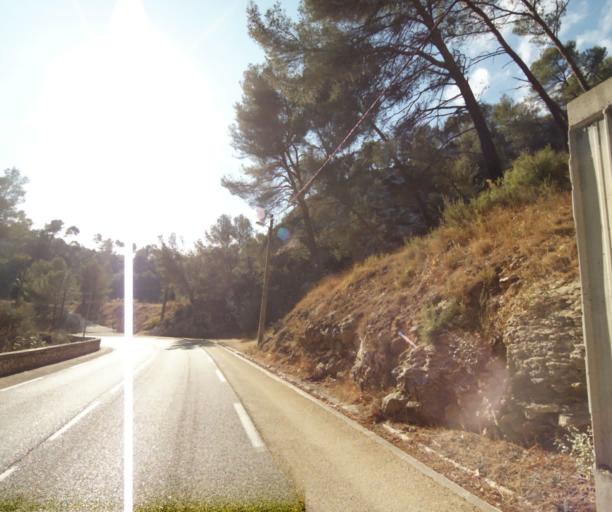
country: FR
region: Provence-Alpes-Cote d'Azur
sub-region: Departement des Bouches-du-Rhone
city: Allauch
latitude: 43.3674
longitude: 5.5019
